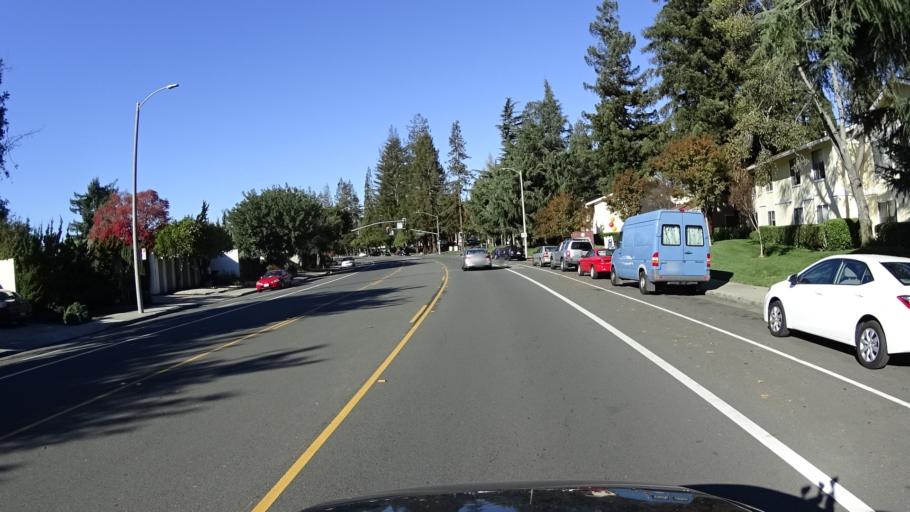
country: US
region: California
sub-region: Santa Clara County
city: Sunnyvale
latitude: 37.3676
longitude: -122.0037
